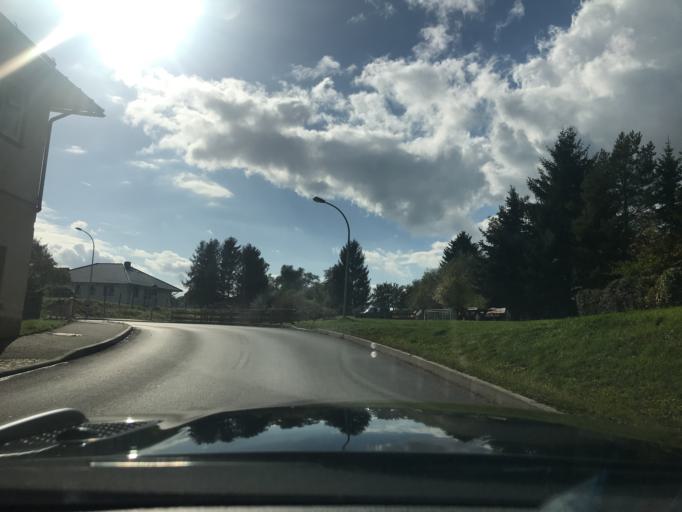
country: DE
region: Thuringia
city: Niederdorla
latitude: 51.1604
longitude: 10.4421
